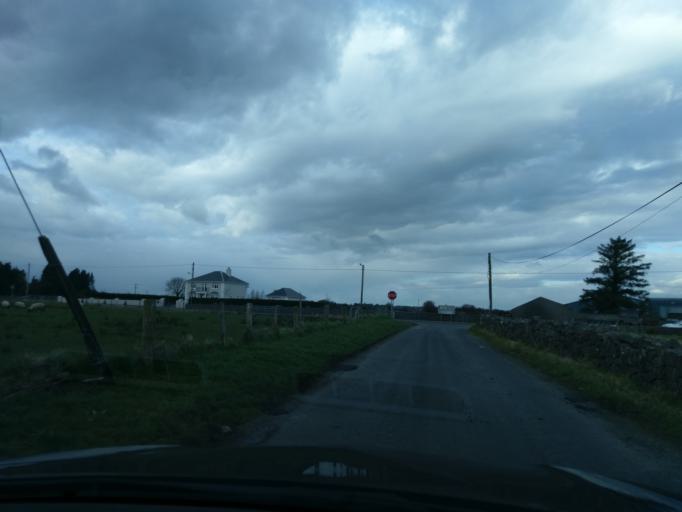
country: IE
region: Connaught
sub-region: County Galway
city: Athenry
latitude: 53.4221
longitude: -8.5828
